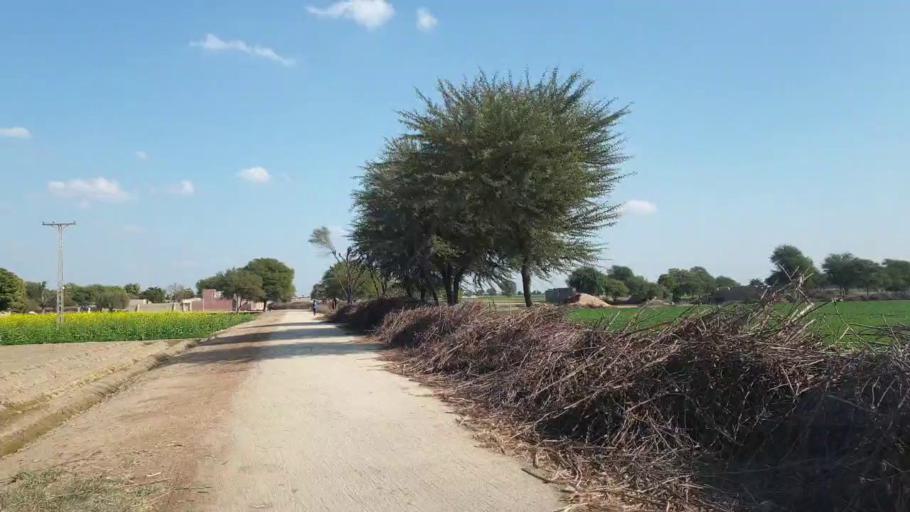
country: PK
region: Sindh
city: Shahpur Chakar
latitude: 26.1023
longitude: 68.5736
